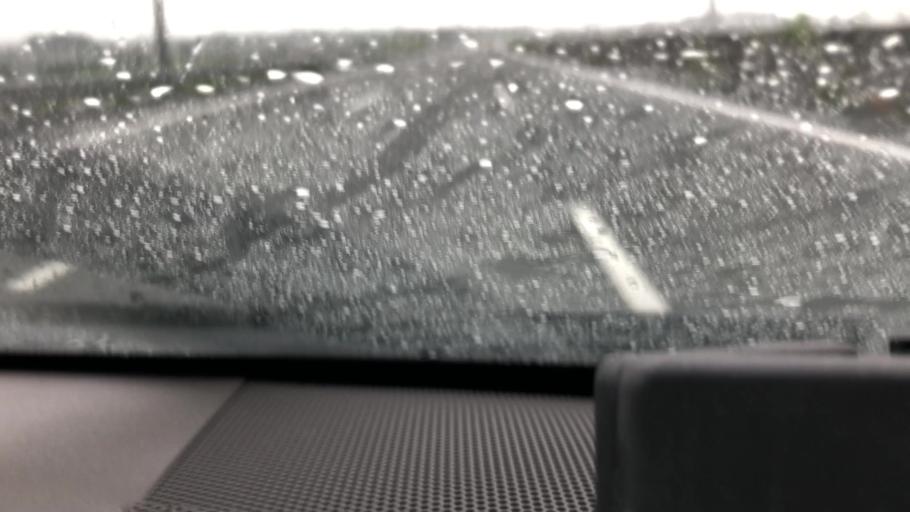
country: JP
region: Shizuoka
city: Fuji
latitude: 35.2026
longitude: 138.6625
